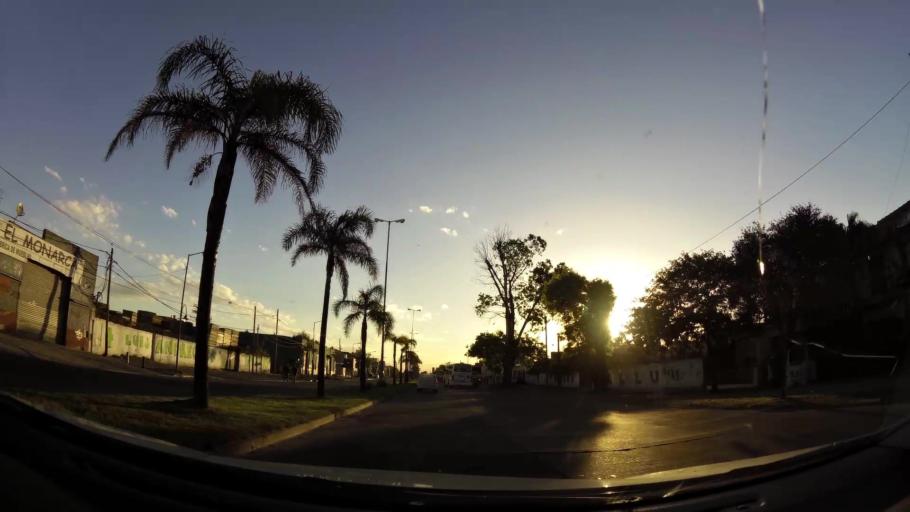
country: AR
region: Buenos Aires
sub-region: Partido de Tigre
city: Tigre
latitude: -34.4397
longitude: -58.5731
